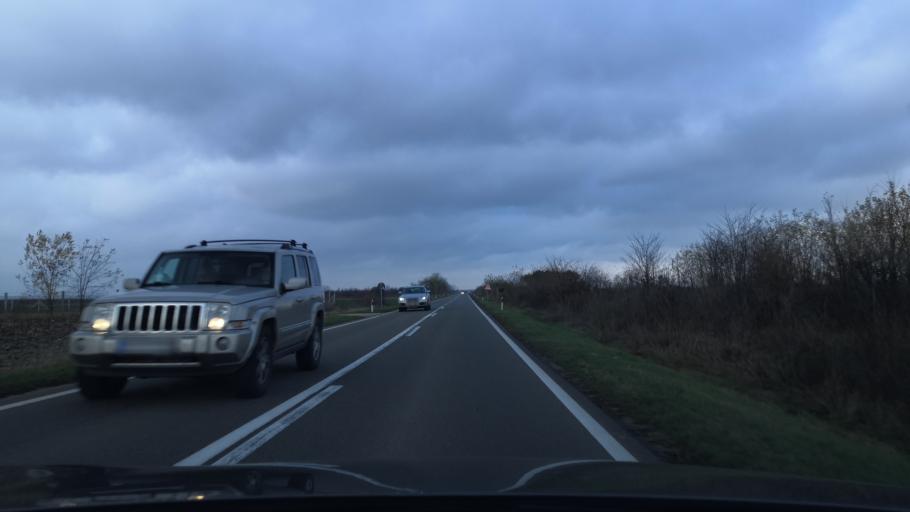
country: RS
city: Sanad
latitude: 45.9901
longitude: 20.1086
